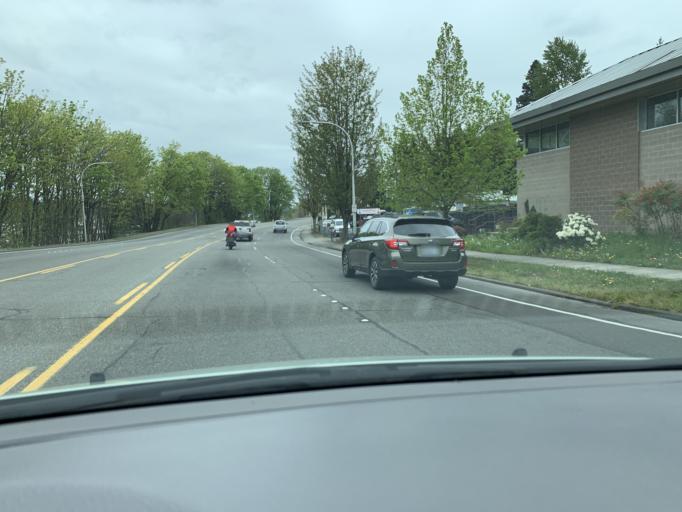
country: US
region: Washington
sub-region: King County
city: Renton
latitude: 47.4914
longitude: -122.2182
